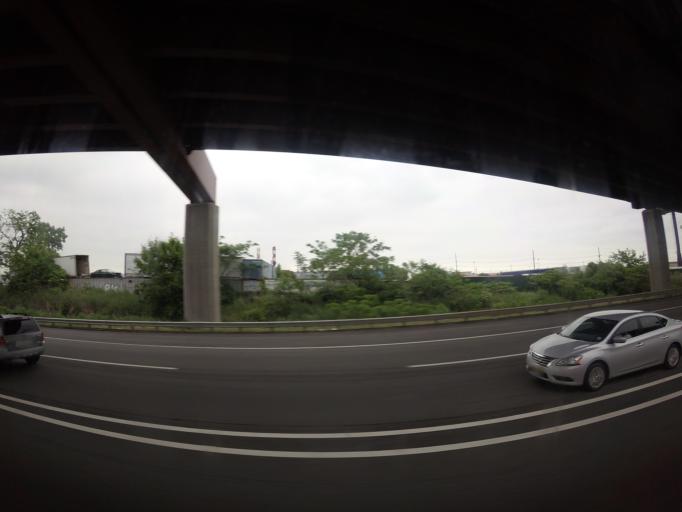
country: US
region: New Jersey
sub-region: Hudson County
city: Harrison
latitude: 40.7196
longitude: -74.1341
